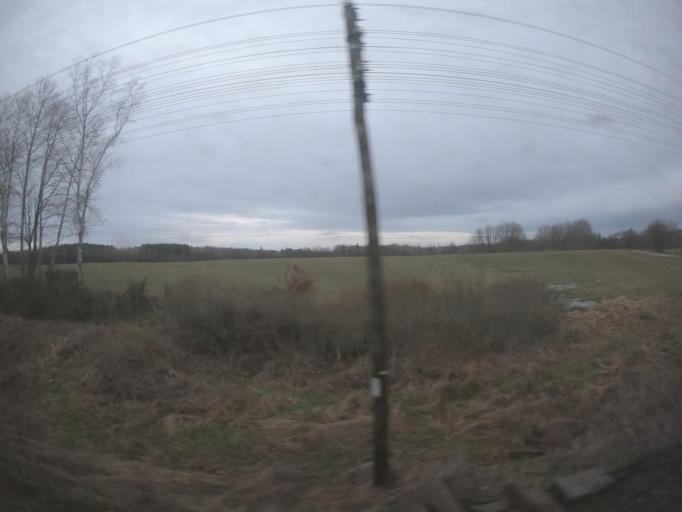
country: PL
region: West Pomeranian Voivodeship
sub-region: Powiat szczecinecki
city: Borne Sulinowo
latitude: 53.6566
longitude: 16.5434
